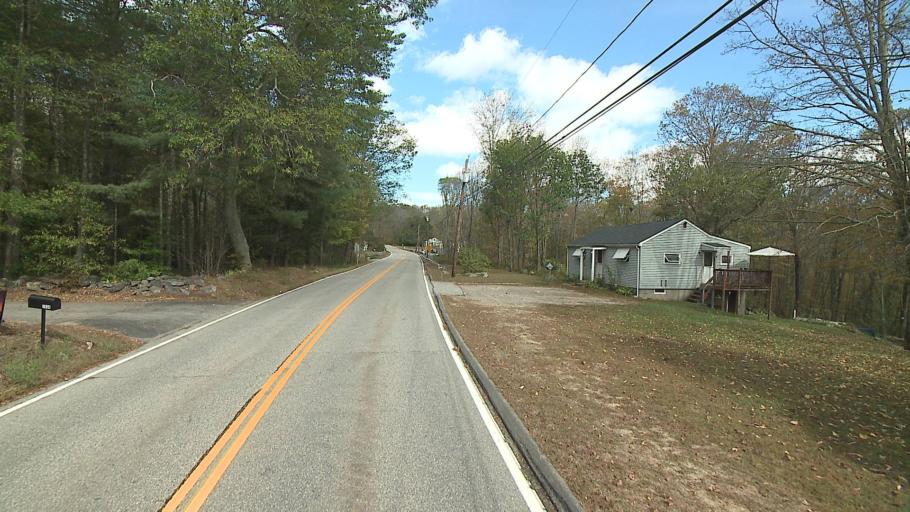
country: US
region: Connecticut
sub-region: Windham County
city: North Grosvenor Dale
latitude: 42.0148
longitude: -71.8877
